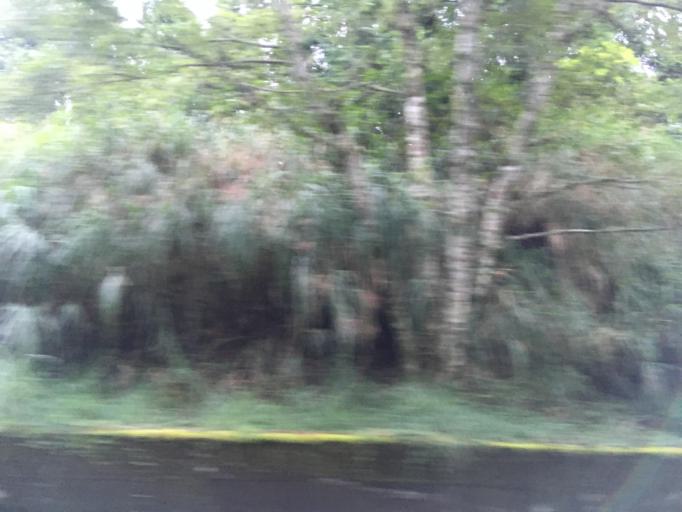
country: TW
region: Taiwan
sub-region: Yilan
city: Yilan
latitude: 24.5119
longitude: 121.5897
